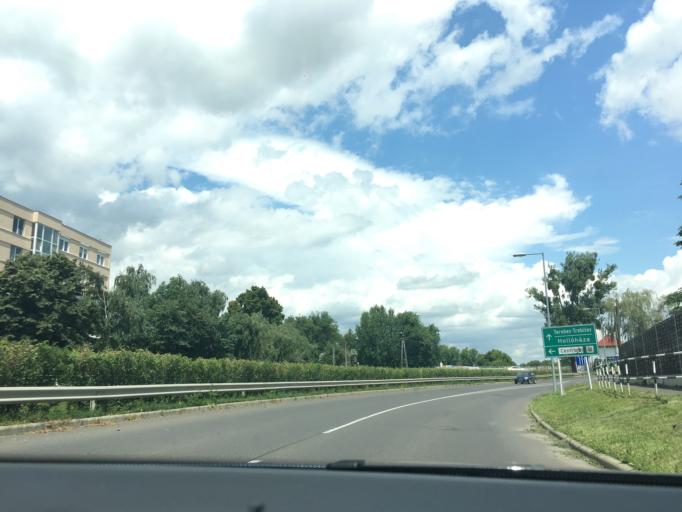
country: HU
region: Borsod-Abauj-Zemplen
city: Satoraljaujhely
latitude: 48.3987
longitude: 21.6617
